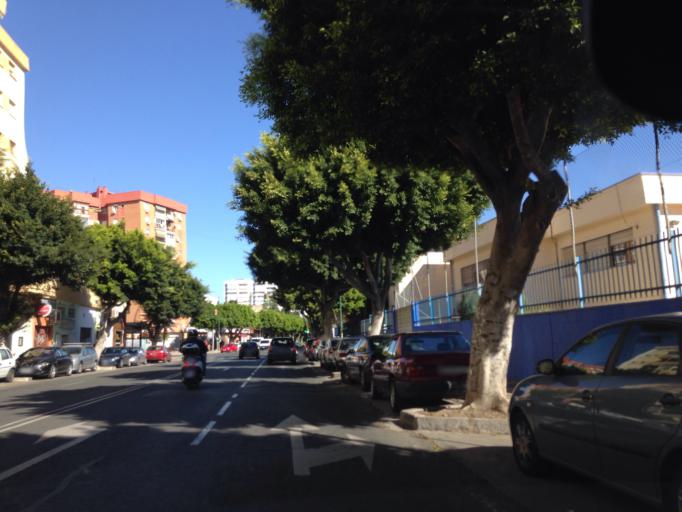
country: ES
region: Andalusia
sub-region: Provincia de Malaga
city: Malaga
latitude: 36.6901
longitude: -4.4474
